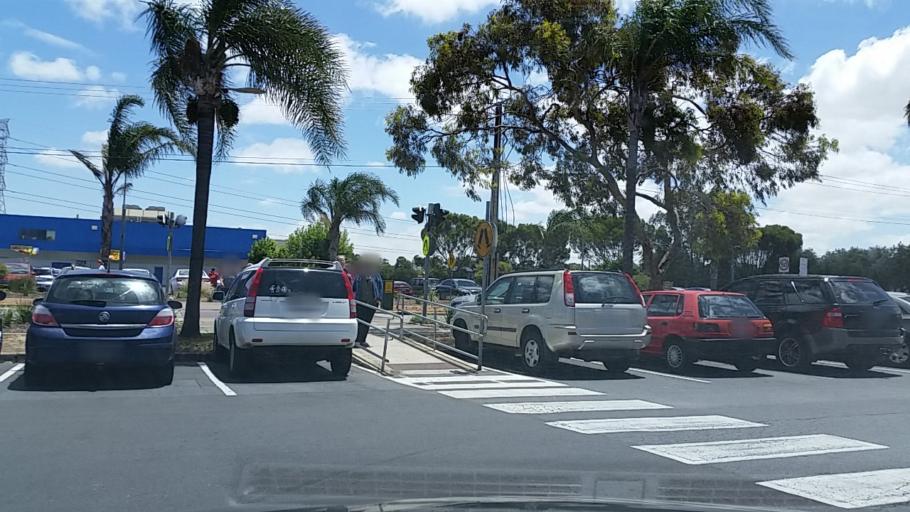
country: AU
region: South Australia
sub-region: Salisbury
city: Salisbury
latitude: -34.7673
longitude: 138.6243
